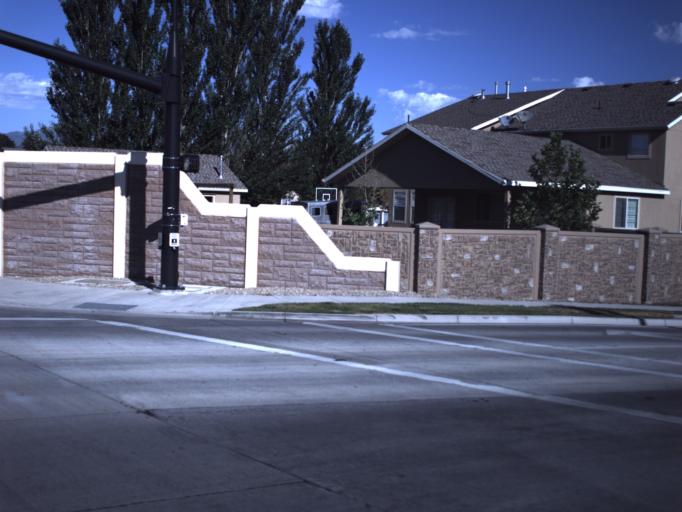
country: US
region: Utah
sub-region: Salt Lake County
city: South Jordan
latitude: 40.5443
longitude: -111.9178
